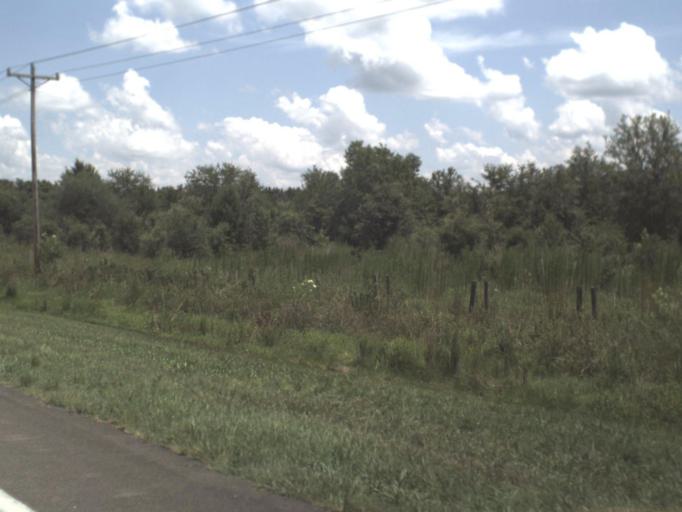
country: US
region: Florida
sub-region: Alachua County
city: Alachua
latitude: 29.8640
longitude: -82.4083
